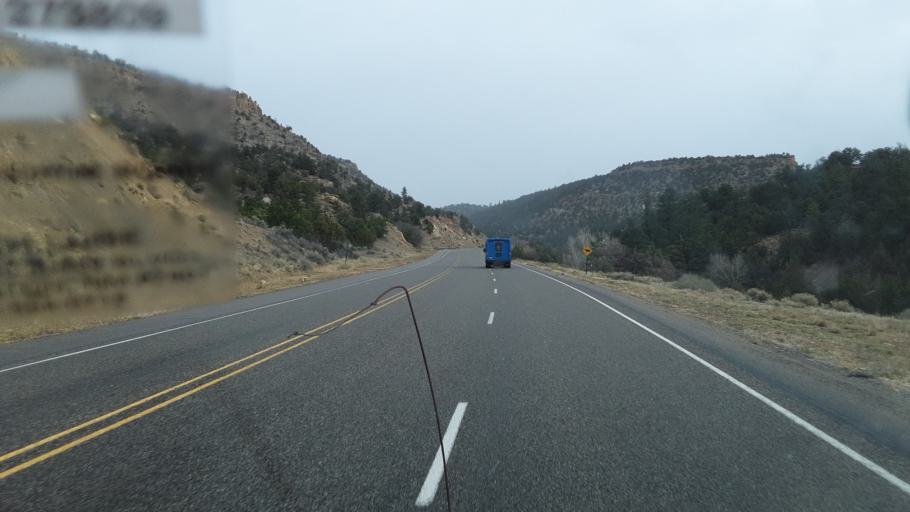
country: US
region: New Mexico
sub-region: Rio Arriba County
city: Tierra Amarilla
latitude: 36.4084
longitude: -106.4872
